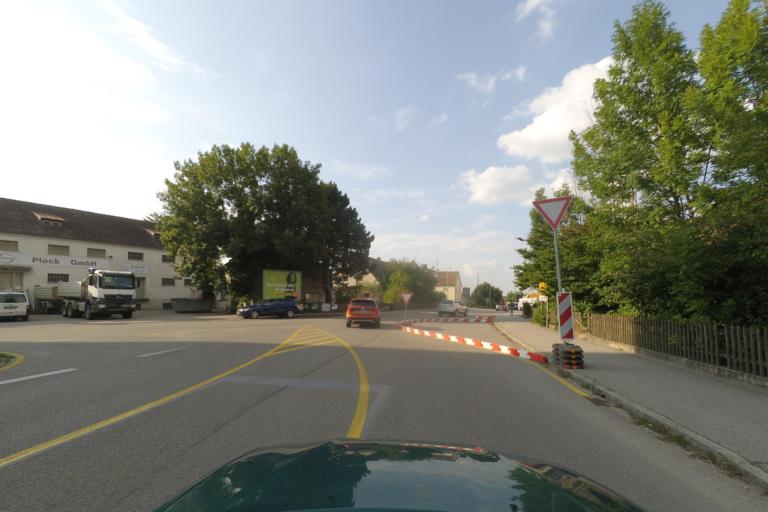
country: DE
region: Bavaria
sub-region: Upper Bavaria
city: Moosburg
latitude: 48.4735
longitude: 11.9329
